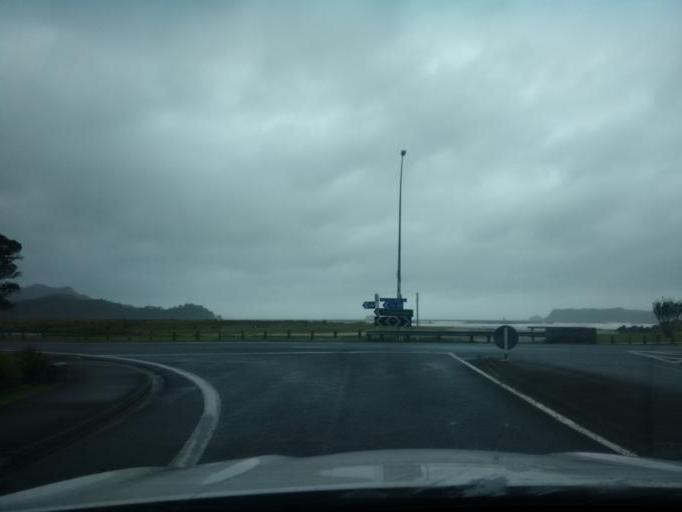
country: NZ
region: Waikato
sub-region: Thames-Coromandel District
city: Whitianga
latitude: -36.8196
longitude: 175.6993
